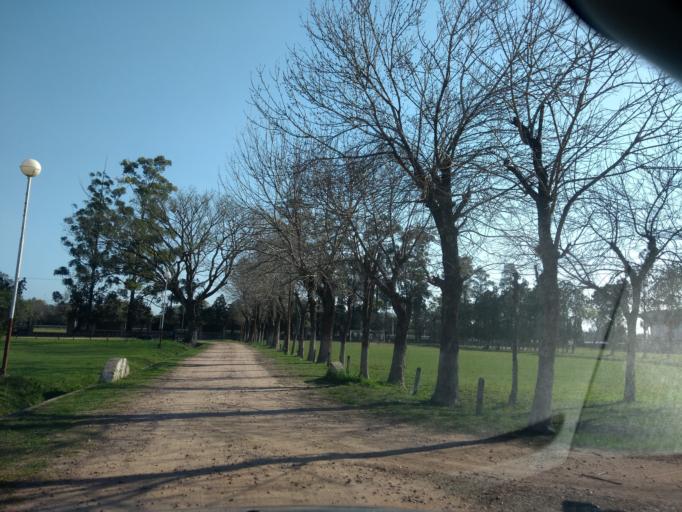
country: AR
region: Chaco
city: Resistencia
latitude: -27.4232
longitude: -58.9481
